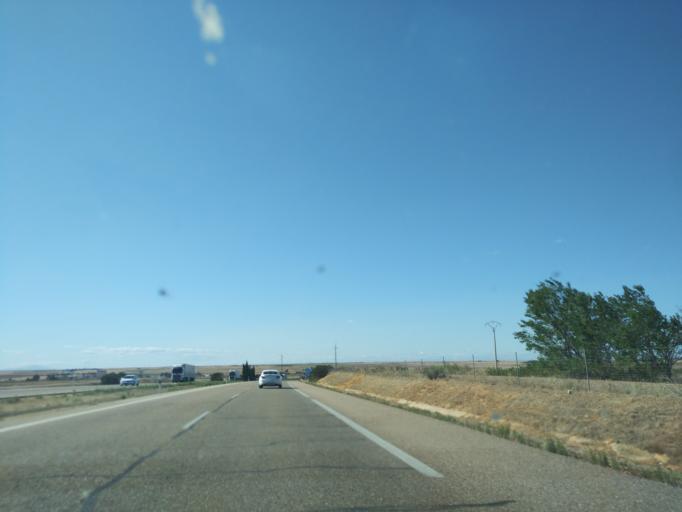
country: ES
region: Castille and Leon
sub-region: Provincia de Zamora
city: Cerecinos de Campos
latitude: 41.8919
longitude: -5.4689
